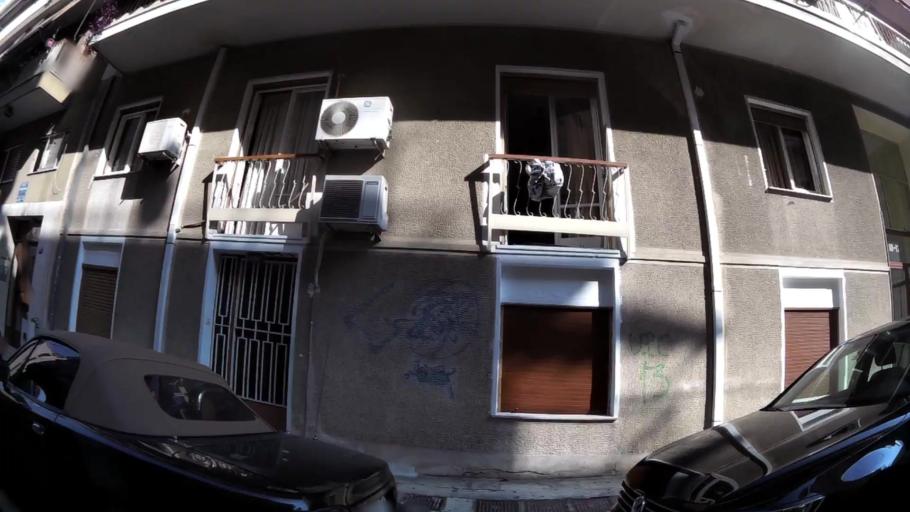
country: GR
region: Attica
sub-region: Nomarchia Athinas
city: Tavros
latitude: 37.9679
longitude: 23.7054
